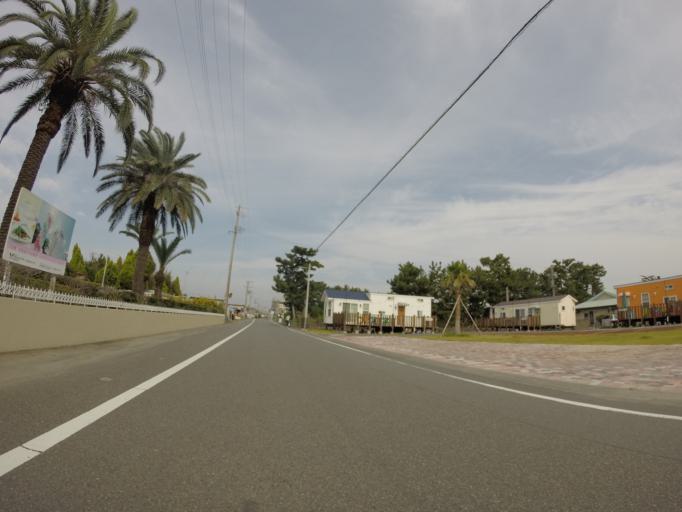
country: JP
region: Shizuoka
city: Sagara
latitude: 34.7301
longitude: 138.2283
